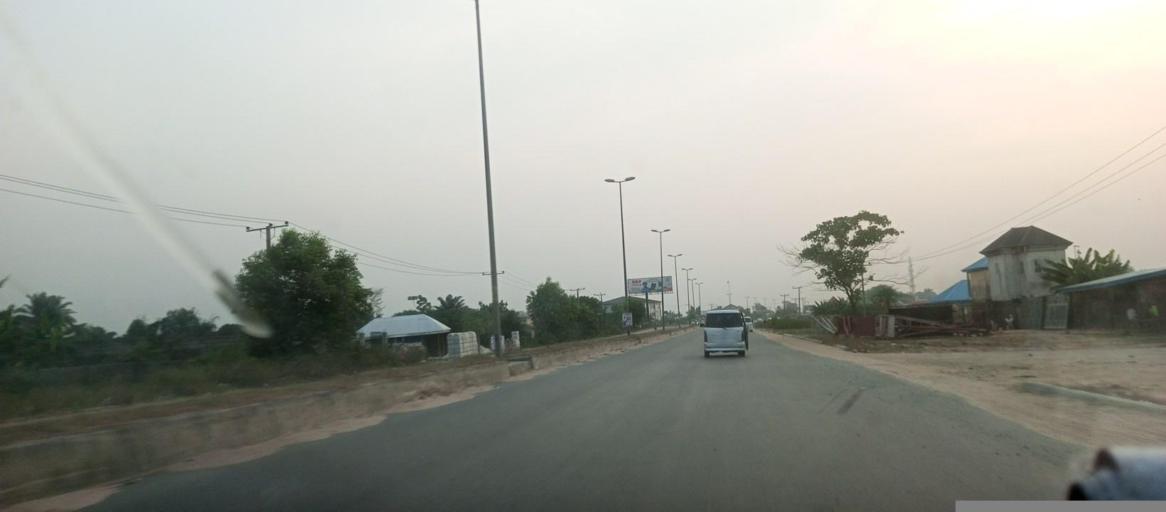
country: NG
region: Rivers
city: Emuoha
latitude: 4.9375
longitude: 7.0067
